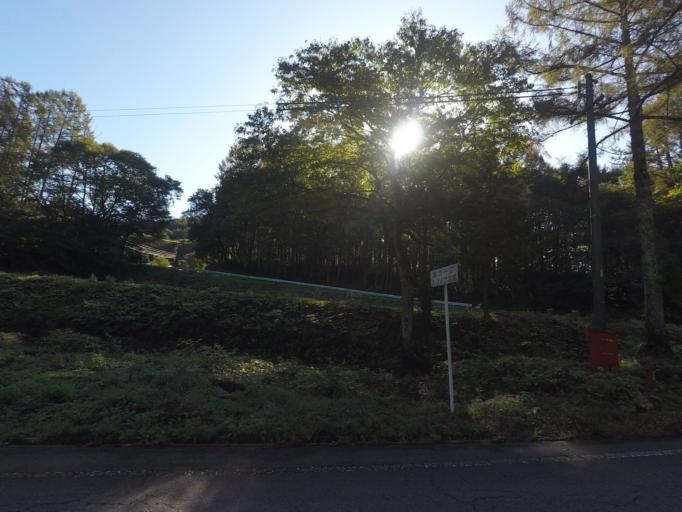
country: JP
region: Nagano
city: Ina
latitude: 35.9646
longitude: 137.7501
